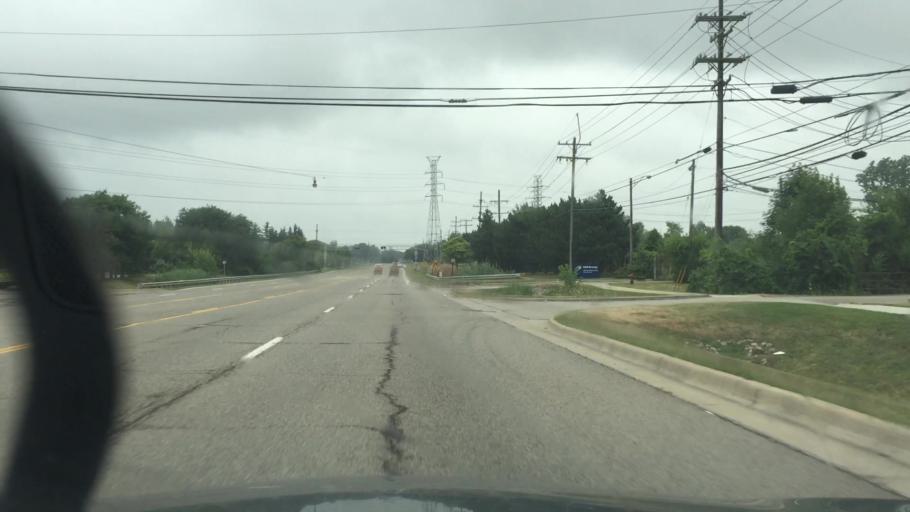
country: US
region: Michigan
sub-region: Oakland County
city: Wixom
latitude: 42.5134
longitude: -83.5370
